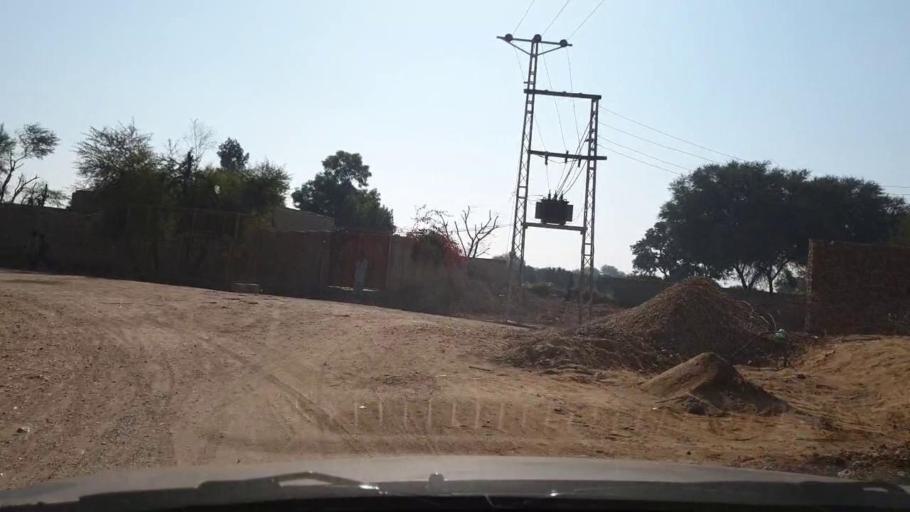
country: PK
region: Sindh
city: Jhol
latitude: 25.9392
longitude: 68.8201
